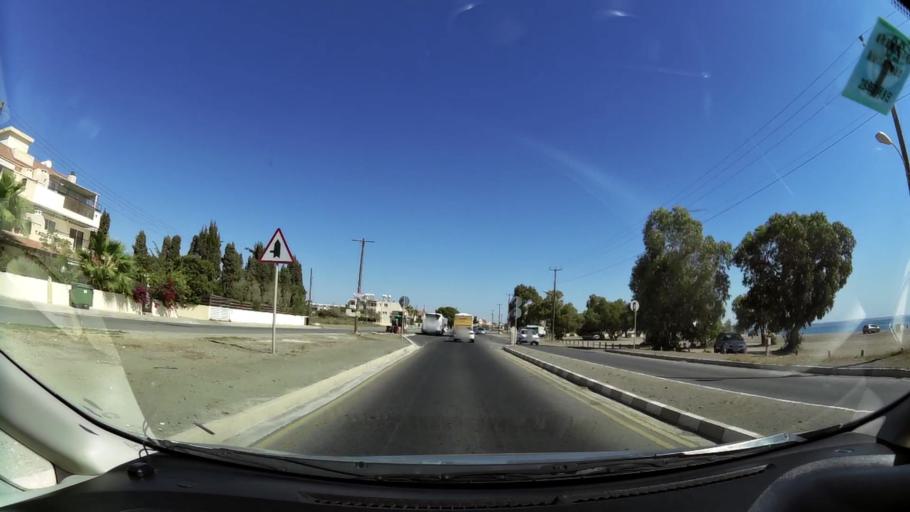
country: CY
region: Larnaka
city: Livadia
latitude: 34.9551
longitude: 33.6521
